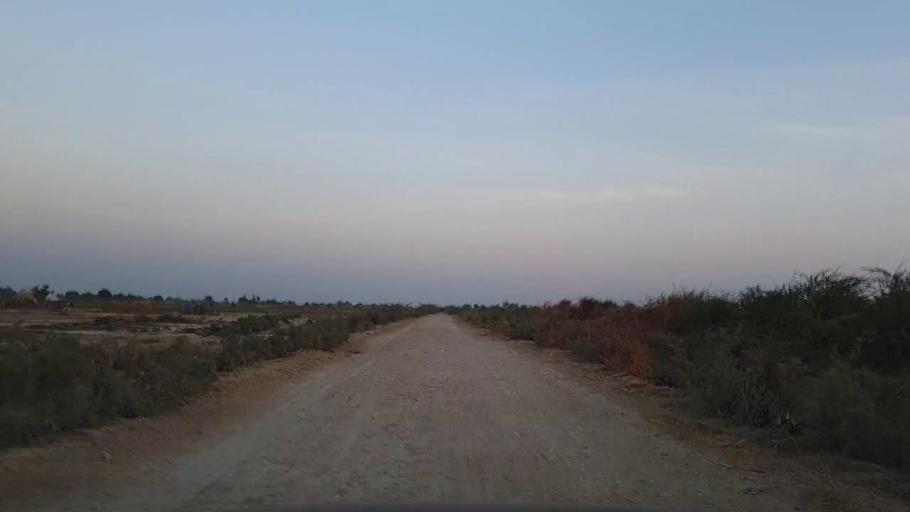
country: PK
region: Sindh
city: Tando Mittha Khan
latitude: 25.9410
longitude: 69.1411
